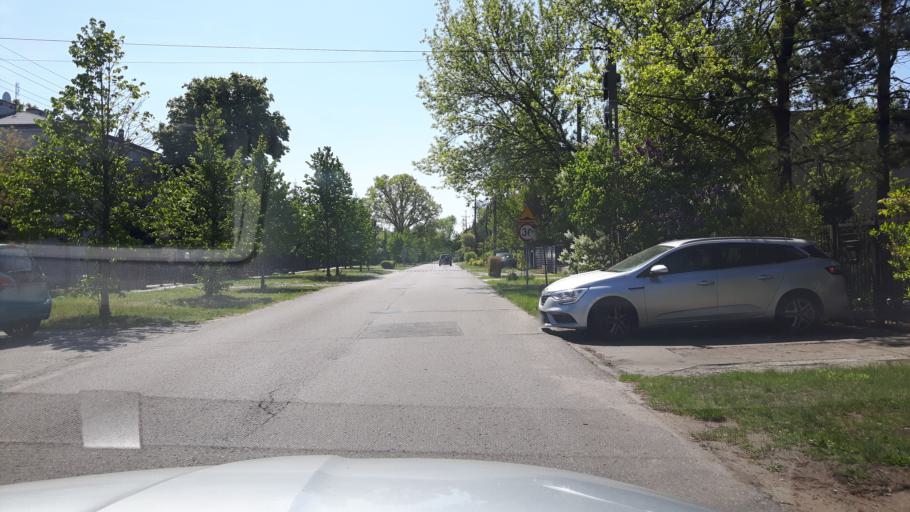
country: PL
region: Masovian Voivodeship
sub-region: Warszawa
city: Rembertow
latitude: 52.2309
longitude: 21.1524
